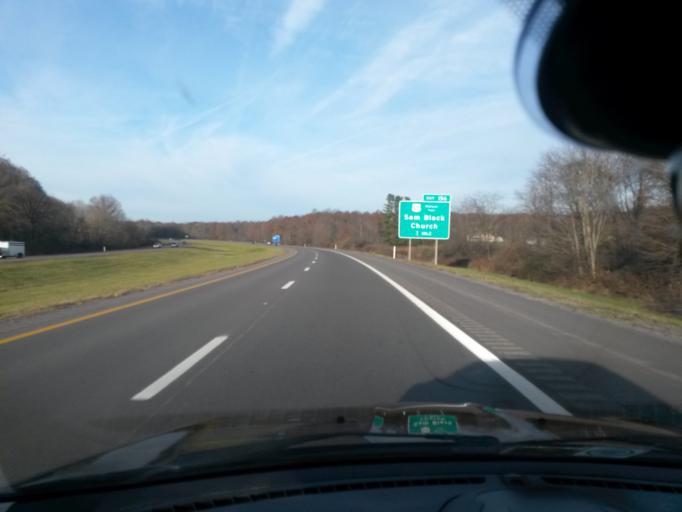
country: US
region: West Virginia
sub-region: Greenbrier County
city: Rainelle
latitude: 37.9075
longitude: -80.6111
